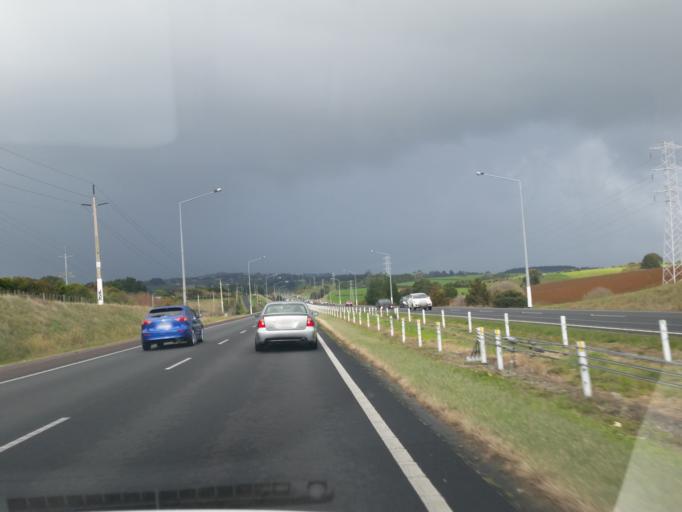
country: NZ
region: Auckland
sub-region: Auckland
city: Pukekohe East
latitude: -37.1483
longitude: 174.9727
